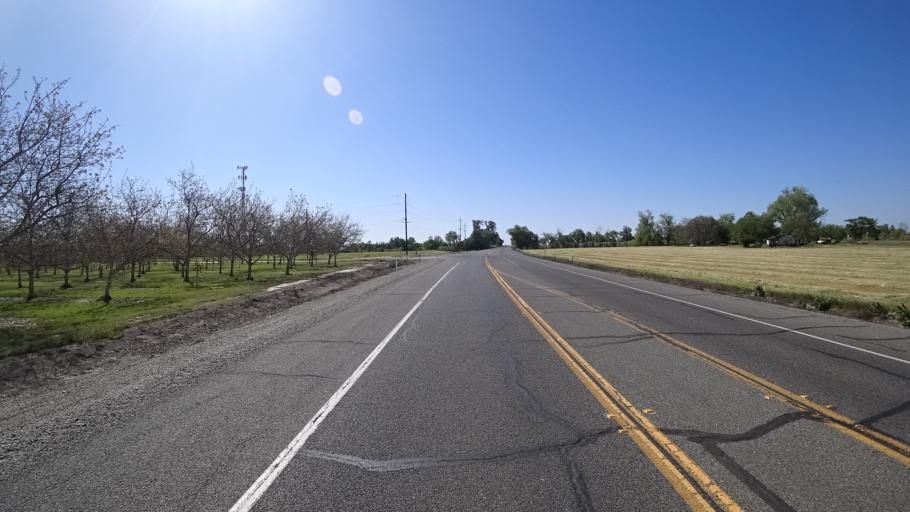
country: US
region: California
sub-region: Glenn County
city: Hamilton City
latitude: 39.7136
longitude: -122.0052
